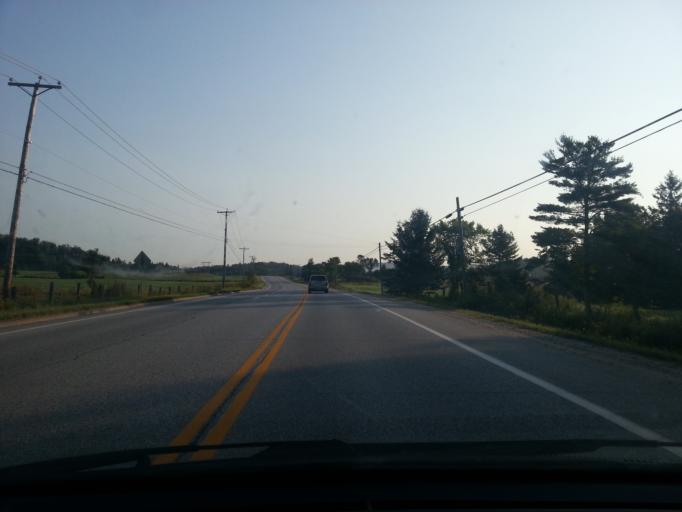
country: CA
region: Quebec
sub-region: Outaouais
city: Wakefield
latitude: 45.7920
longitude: -75.9490
